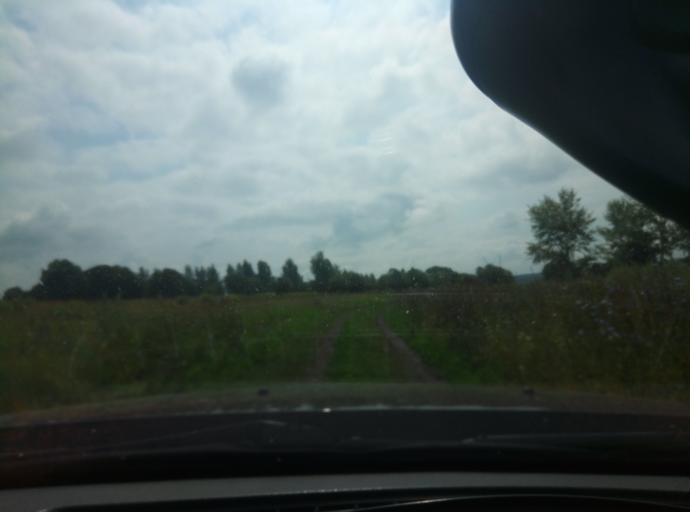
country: RU
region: Tula
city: Shvartsevskiy
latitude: 54.0805
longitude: 38.0214
